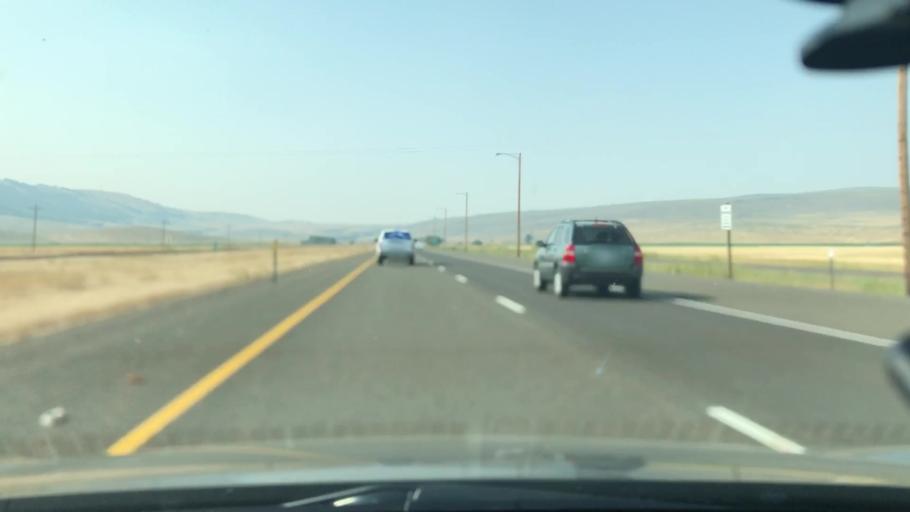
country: US
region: Oregon
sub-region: Union County
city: Union
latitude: 45.1041
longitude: -117.9554
